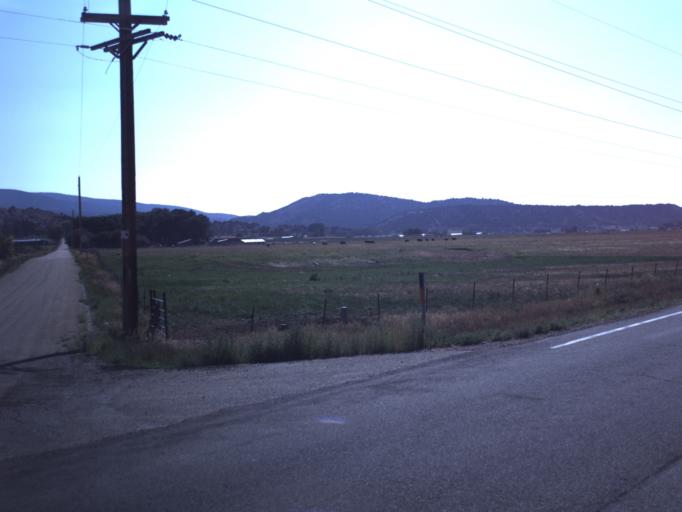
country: US
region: Utah
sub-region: Duchesne County
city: Duchesne
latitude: 40.3714
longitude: -110.7269
